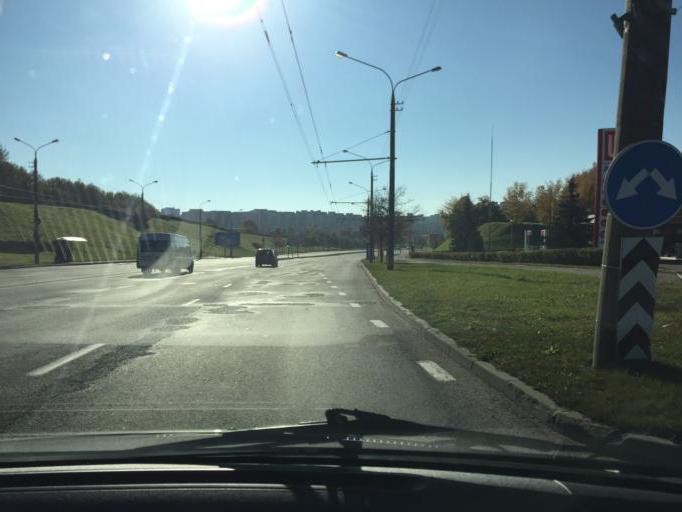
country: BY
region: Minsk
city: Syenitsa
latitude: 53.8595
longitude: 27.5376
